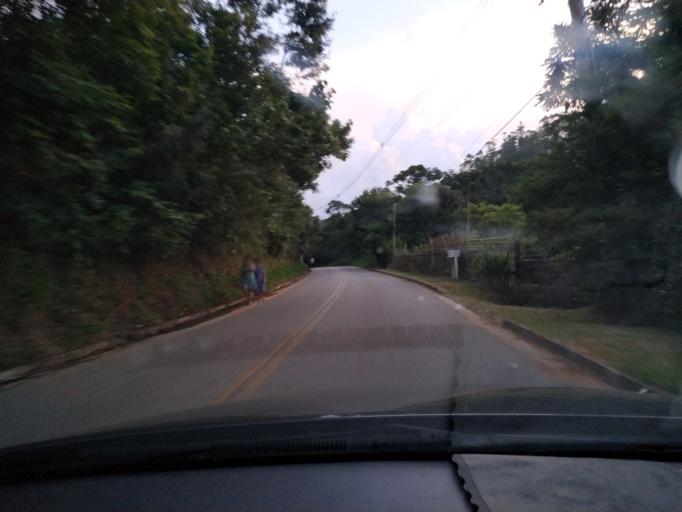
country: BR
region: Sao Paulo
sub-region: Campos Do Jordao
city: Campos do Jordao
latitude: -22.8164
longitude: -45.6636
